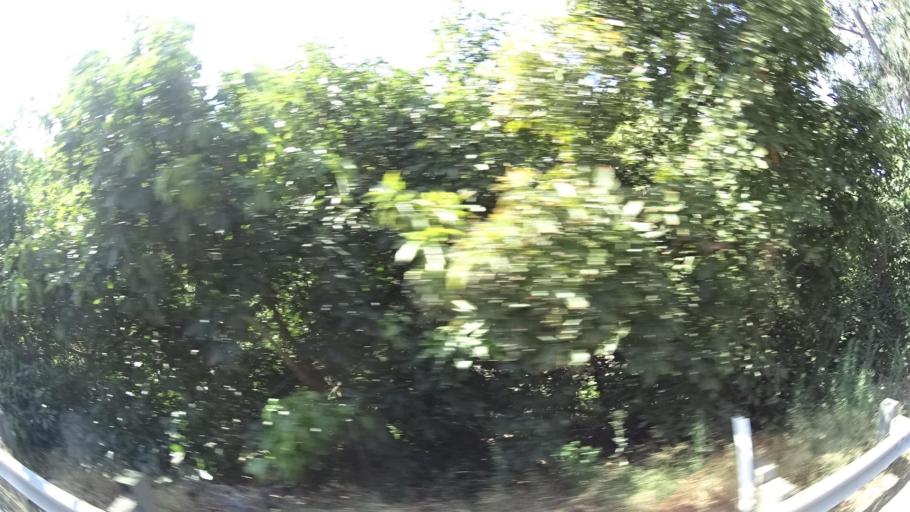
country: US
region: California
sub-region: San Diego County
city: Hidden Meadows
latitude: 33.1947
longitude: -117.1314
